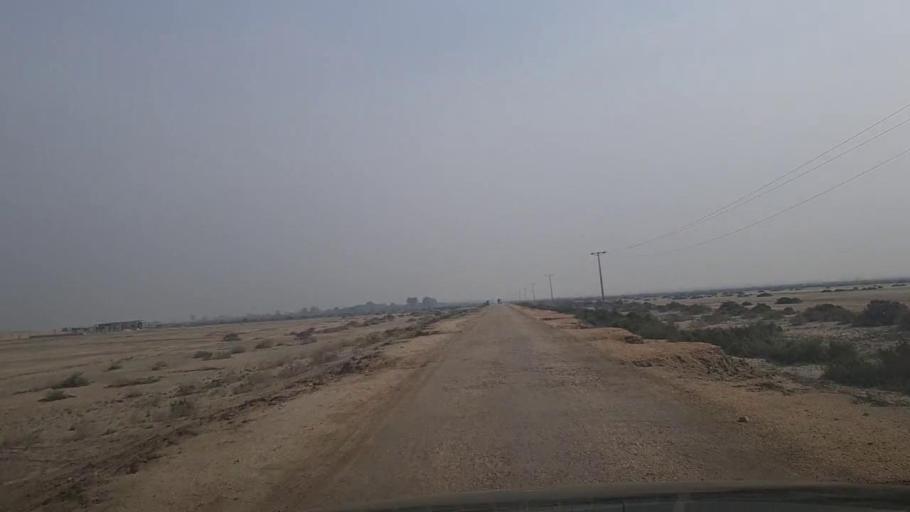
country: PK
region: Sindh
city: Mirpur Sakro
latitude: 24.4638
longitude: 67.6883
